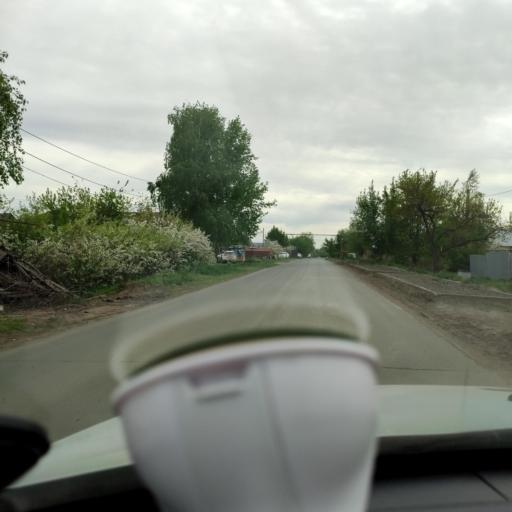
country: RU
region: Samara
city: Smyshlyayevka
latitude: 53.2218
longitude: 50.3376
